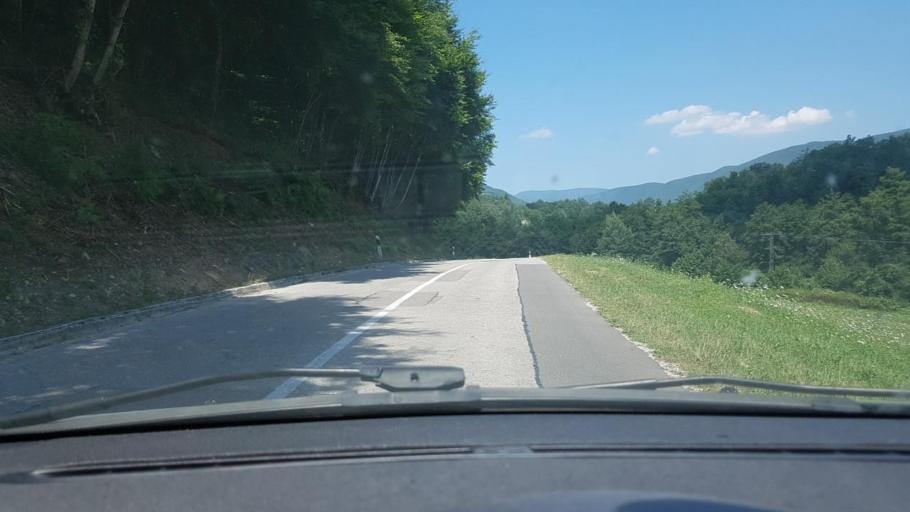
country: BA
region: Federation of Bosnia and Herzegovina
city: Orasac
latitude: 44.6020
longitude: 16.0713
